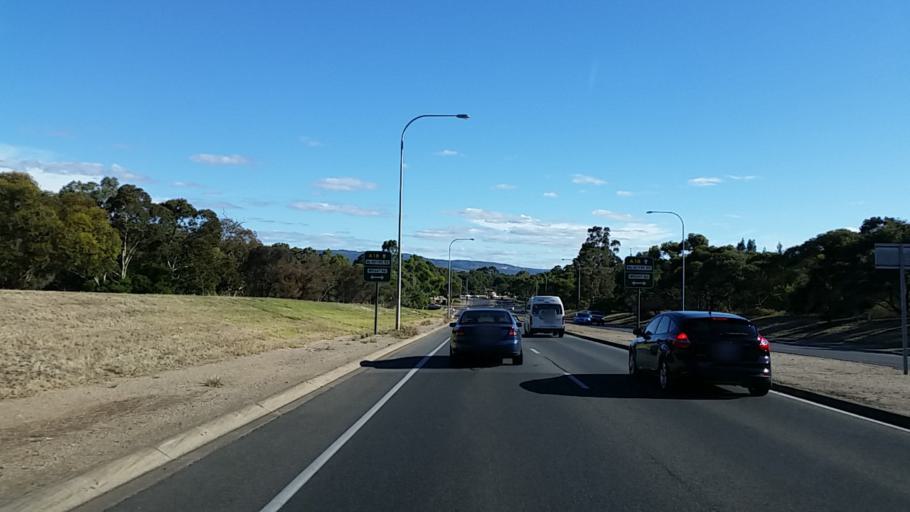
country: AU
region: South Australia
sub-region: Tea Tree Gully
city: Modbury
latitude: -34.8313
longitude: 138.6803
